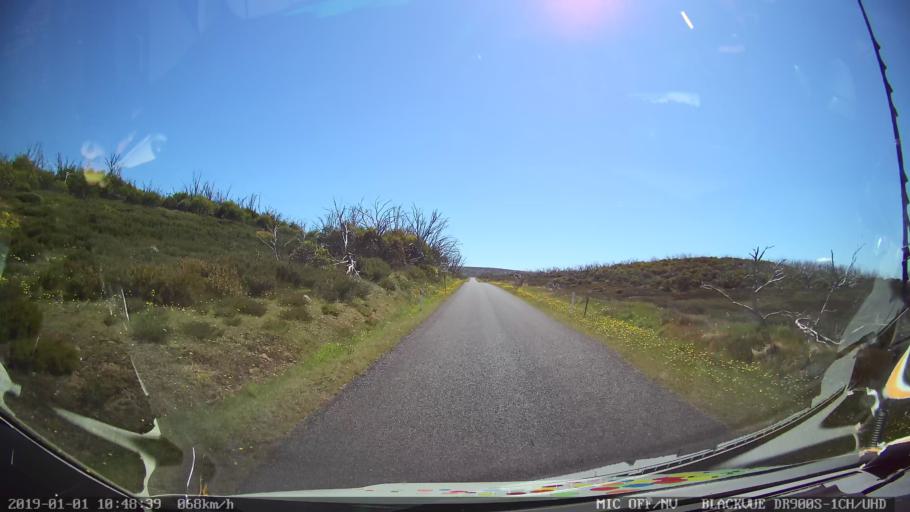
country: AU
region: New South Wales
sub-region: Snowy River
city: Jindabyne
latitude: -36.0386
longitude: 148.3625
